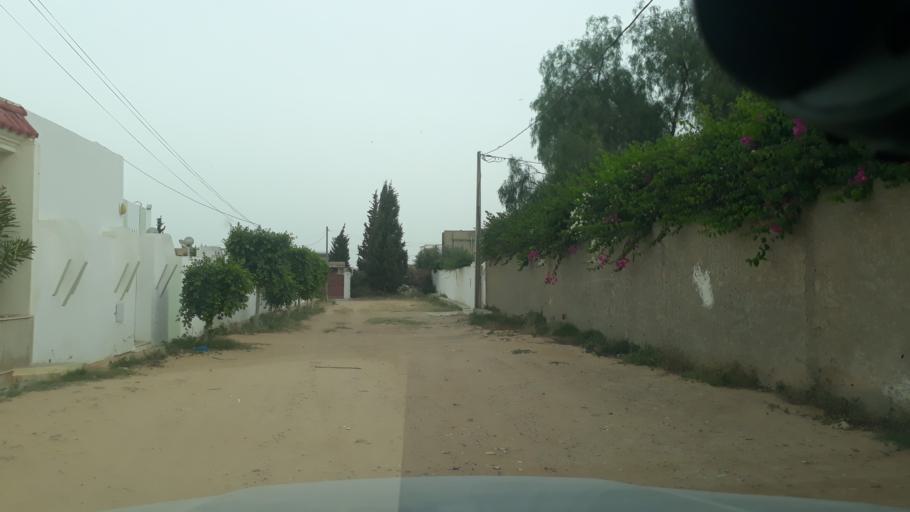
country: TN
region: Safaqis
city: Al Qarmadah
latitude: 34.7821
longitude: 10.7679
